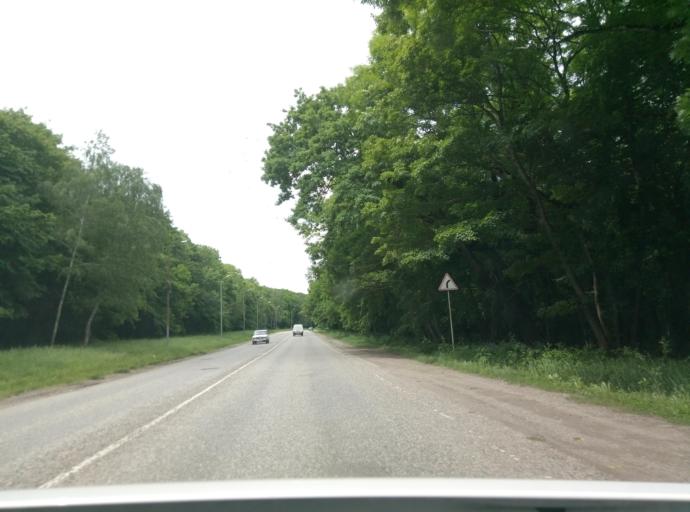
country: RU
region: Stavropol'skiy
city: Novoterskiy
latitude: 44.1264
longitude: 43.0661
